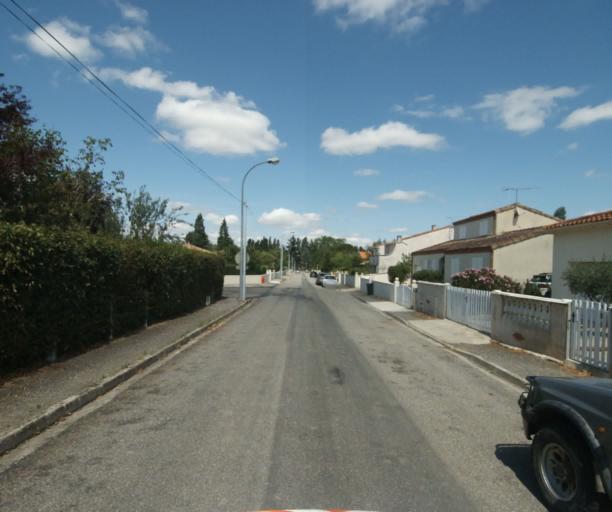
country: FR
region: Midi-Pyrenees
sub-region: Departement de la Haute-Garonne
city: Revel
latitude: 43.4564
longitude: 2.0170
